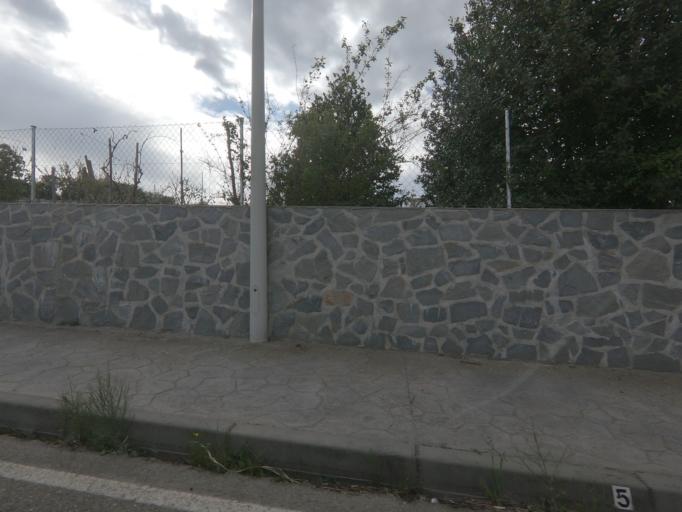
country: ES
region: Castille and Leon
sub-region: Provincia de Salamanca
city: Robleda
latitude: 40.3849
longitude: -6.6098
